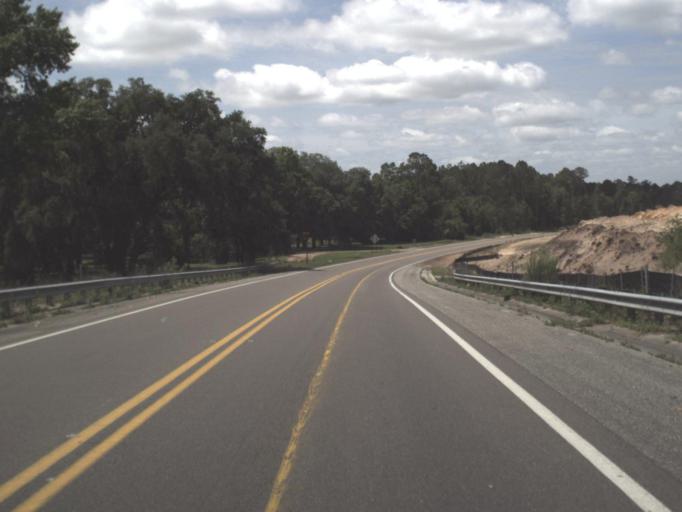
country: US
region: Florida
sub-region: Nassau County
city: Nassau Village-Ratliff
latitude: 30.5073
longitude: -81.8776
